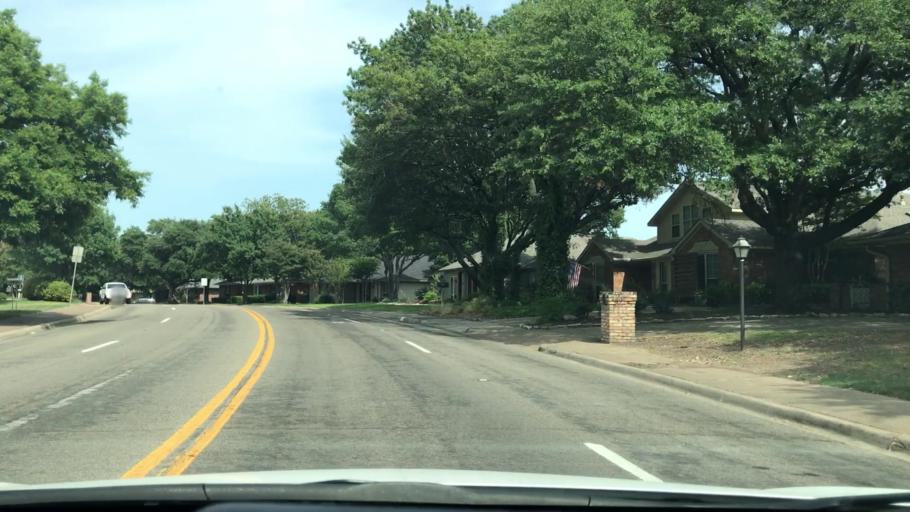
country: US
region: Texas
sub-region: Dallas County
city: University Park
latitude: 32.8864
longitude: -96.7769
